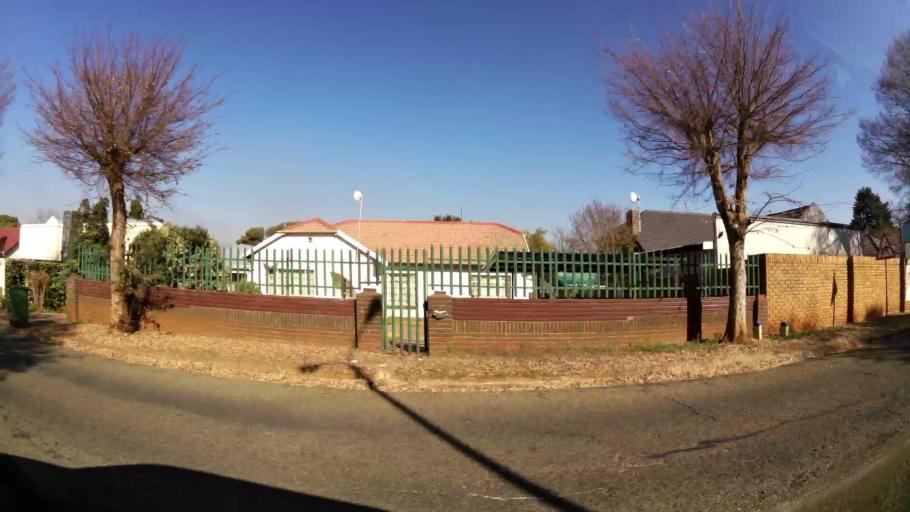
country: ZA
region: Gauteng
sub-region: City of Johannesburg Metropolitan Municipality
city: Modderfontein
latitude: -26.1571
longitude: 28.1546
